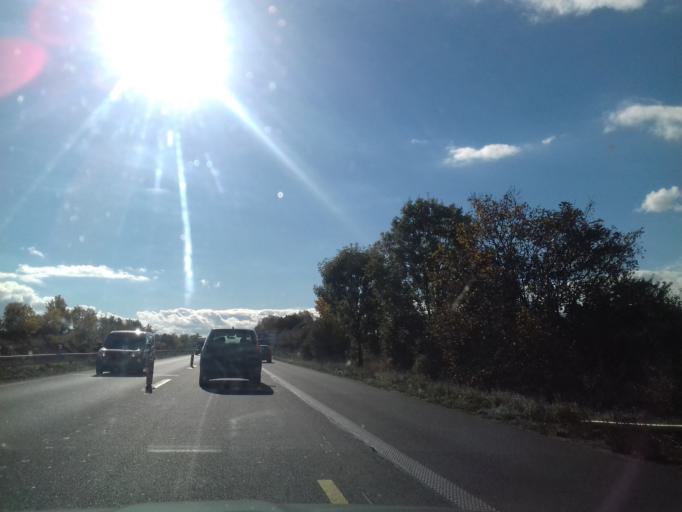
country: CZ
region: Central Bohemia
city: Zelenec
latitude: 50.1488
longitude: 14.6554
